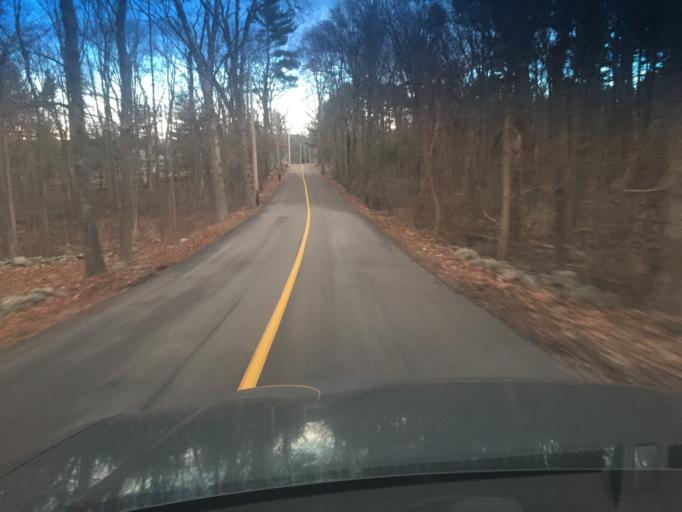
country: US
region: Massachusetts
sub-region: Middlesex County
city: Holliston
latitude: 42.1586
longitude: -71.4417
